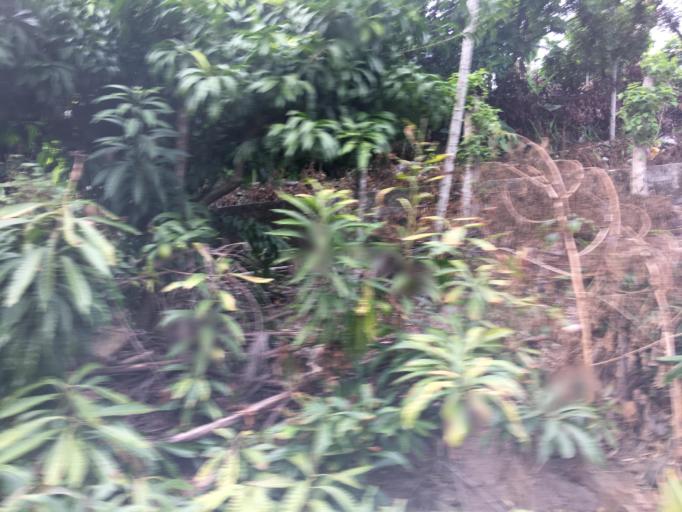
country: TW
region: Taiwan
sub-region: Chiayi
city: Jiayi Shi
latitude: 23.5384
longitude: 120.5616
